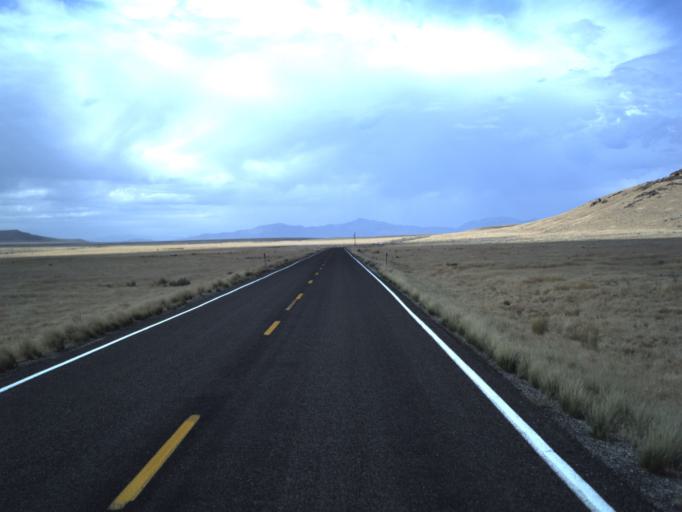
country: US
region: Utah
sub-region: Tooele County
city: Wendover
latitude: 41.3820
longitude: -113.9922
